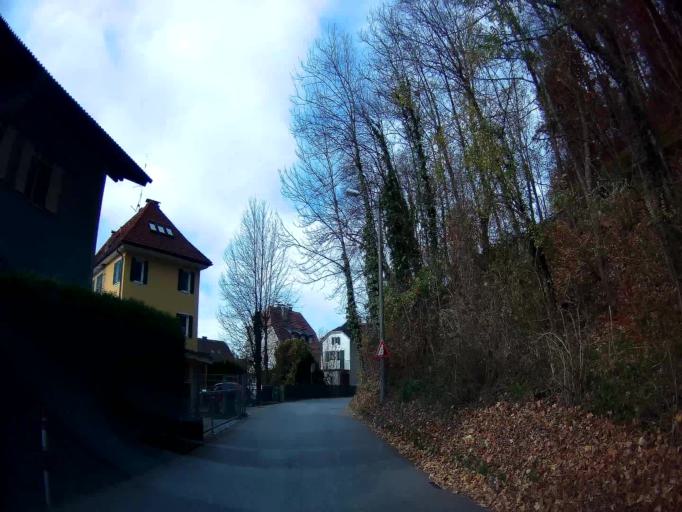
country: AT
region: Salzburg
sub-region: Salzburg Stadt
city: Salzburg
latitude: 47.8080
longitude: 13.0734
